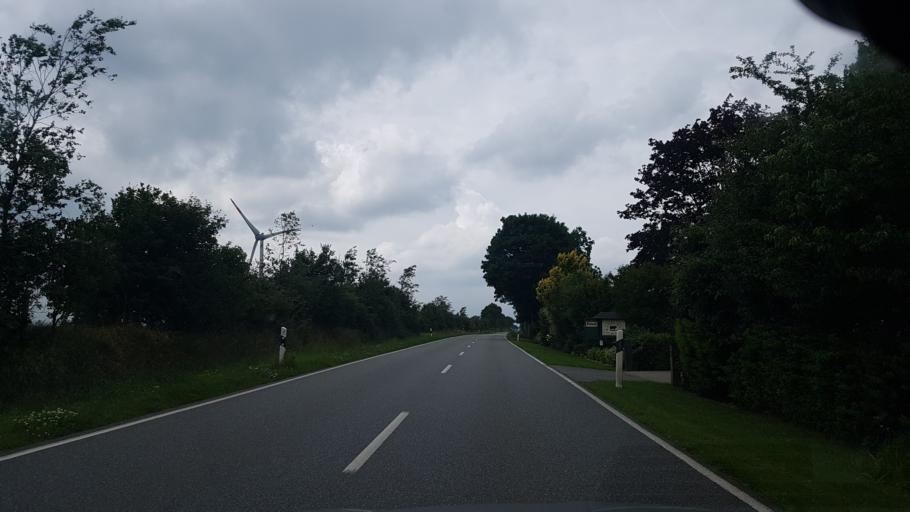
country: DE
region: Schleswig-Holstein
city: Weesby
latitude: 54.8602
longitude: 9.1442
